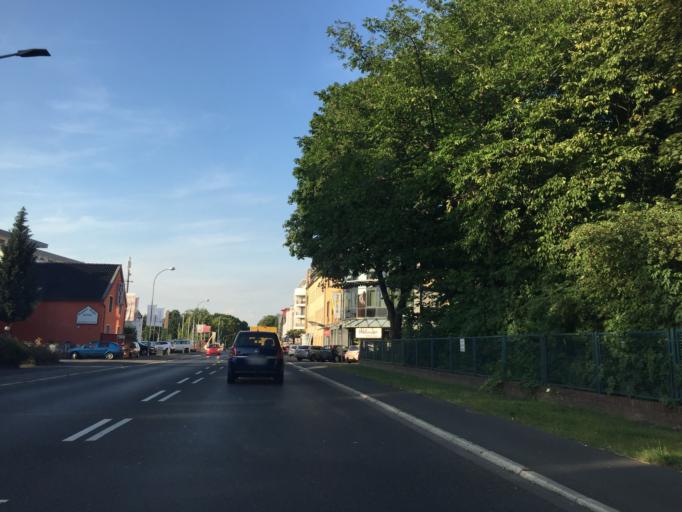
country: DE
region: North Rhine-Westphalia
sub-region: Regierungsbezirk Koln
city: Hurth
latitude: 50.8920
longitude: 6.9027
